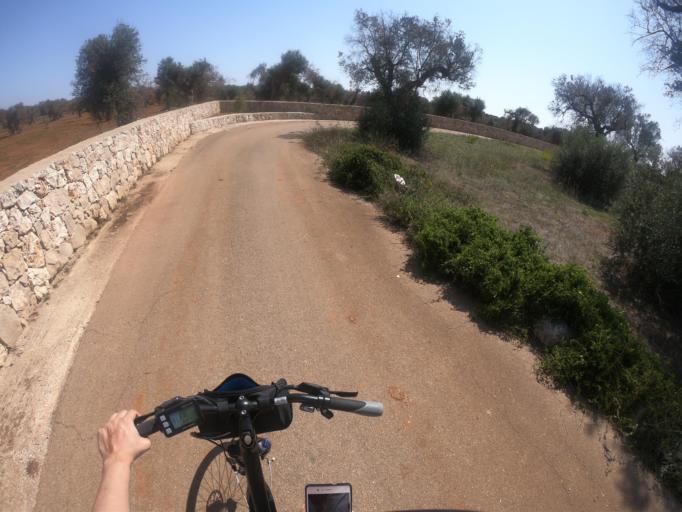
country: IT
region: Apulia
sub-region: Provincia di Lecce
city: Presicce
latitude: 39.9205
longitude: 18.2782
